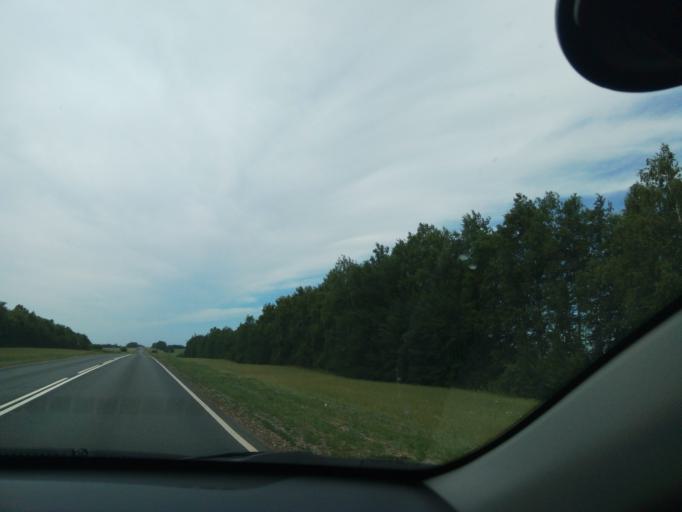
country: RU
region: Tambov
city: Selezni
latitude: 52.6391
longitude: 40.9557
